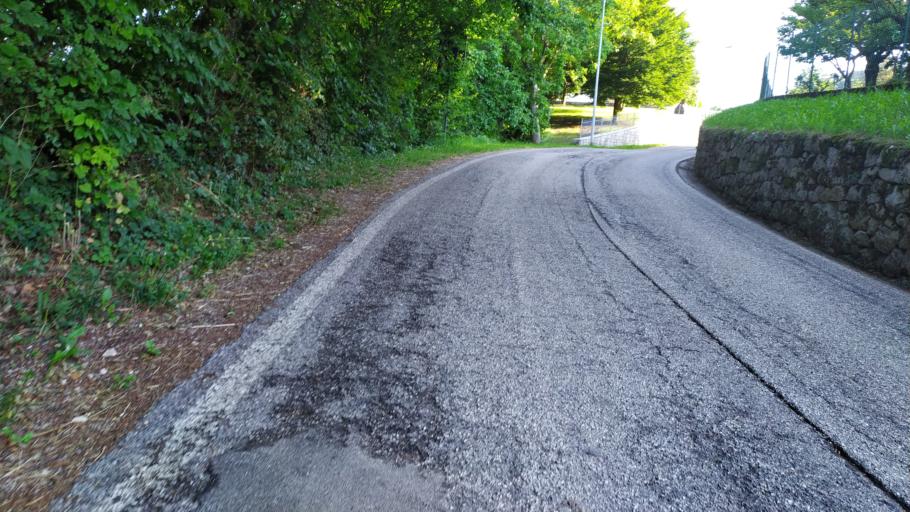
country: IT
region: Veneto
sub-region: Provincia di Vicenza
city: Schio
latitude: 45.6865
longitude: 11.3372
